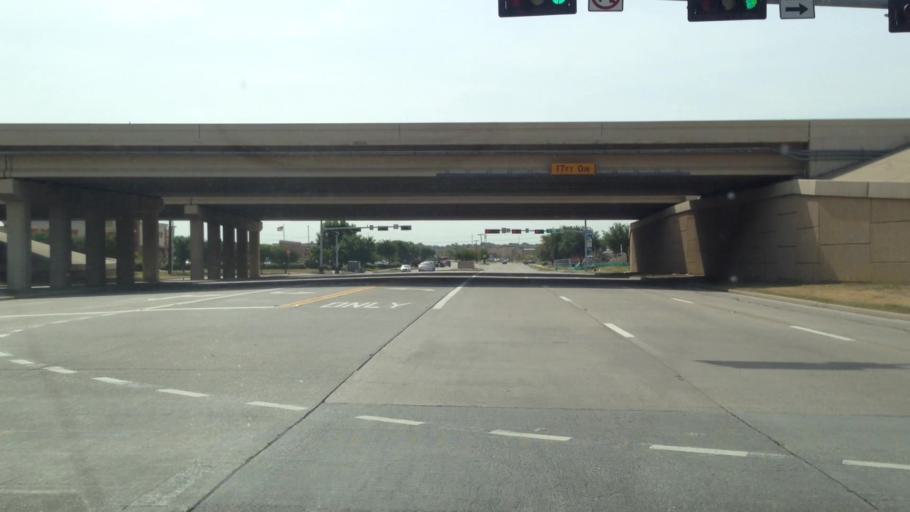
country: US
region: Texas
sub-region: Denton County
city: Lewisville
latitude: 33.0226
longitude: -96.9350
